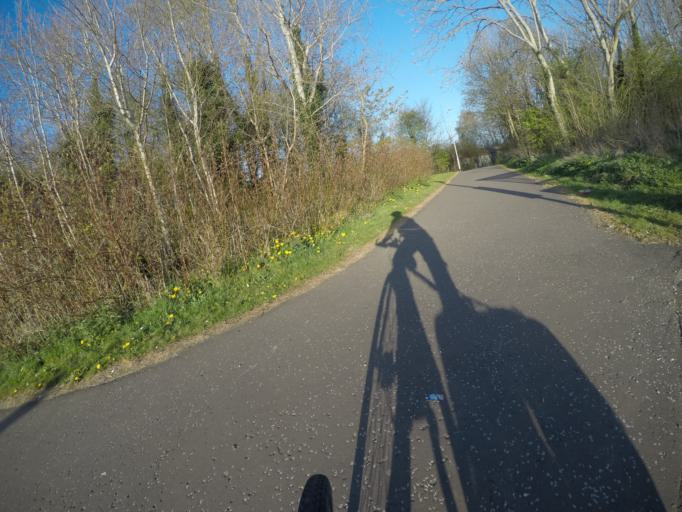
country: GB
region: Scotland
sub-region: North Ayrshire
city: Kilwinning
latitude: 55.6510
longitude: -4.7078
